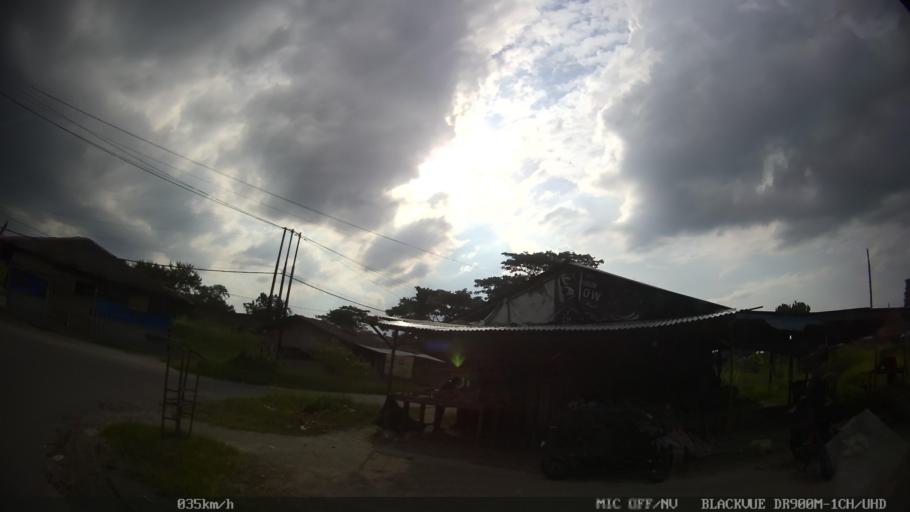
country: ID
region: North Sumatra
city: Sunggal
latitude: 3.5313
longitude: 98.6053
